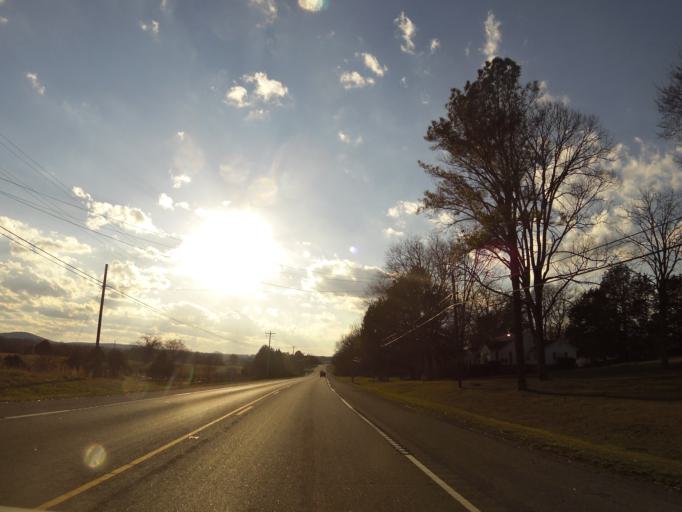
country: US
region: Tennessee
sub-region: Smith County
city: Carthage
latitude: 36.2596
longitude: -86.0803
